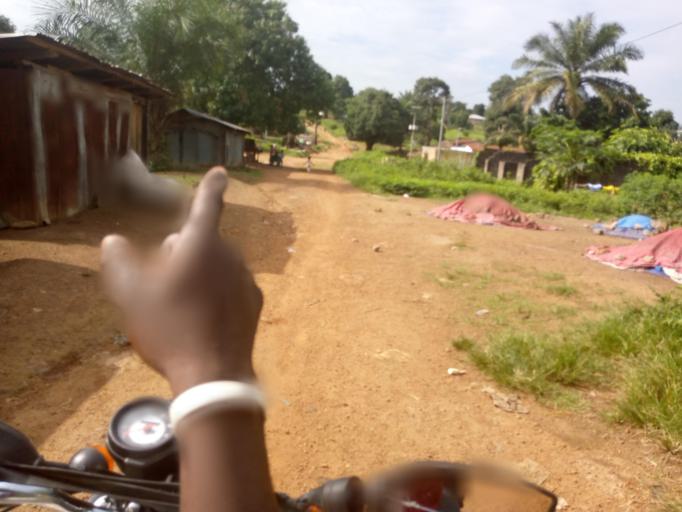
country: SL
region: Eastern Province
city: Buedu
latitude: 8.4561
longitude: -10.3344
